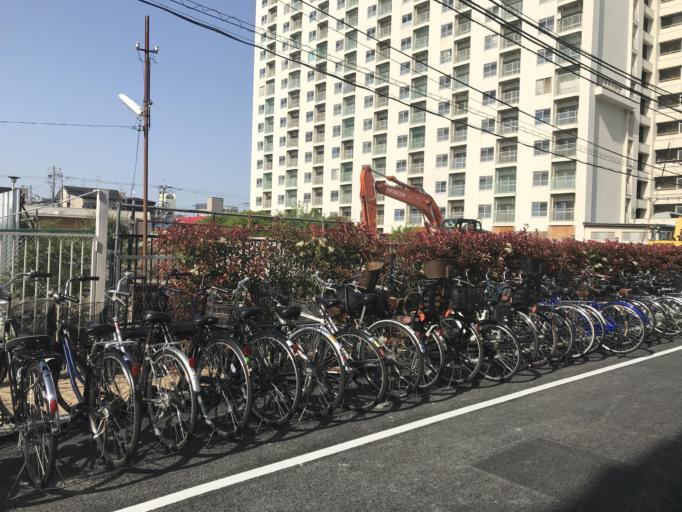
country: JP
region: Osaka
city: Yao
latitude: 34.6519
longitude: 135.5907
